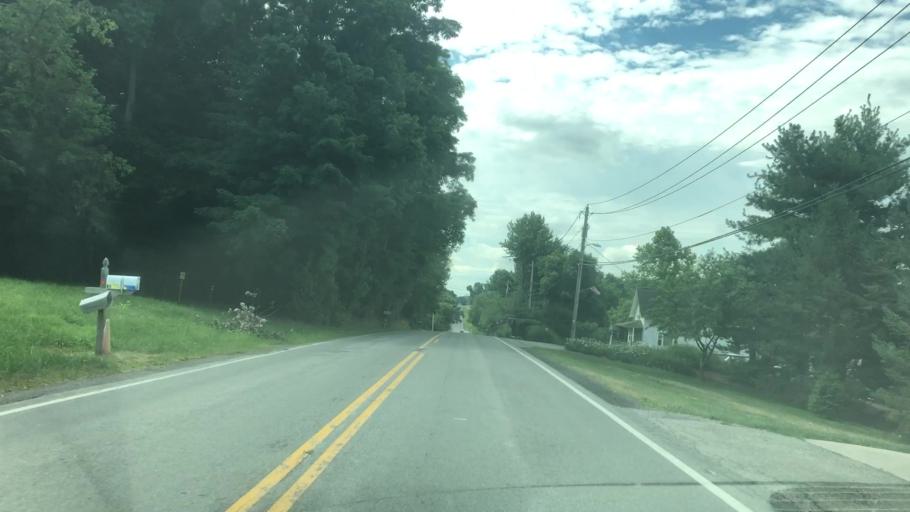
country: US
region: New York
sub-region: Monroe County
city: Fairport
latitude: 43.0771
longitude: -77.3922
